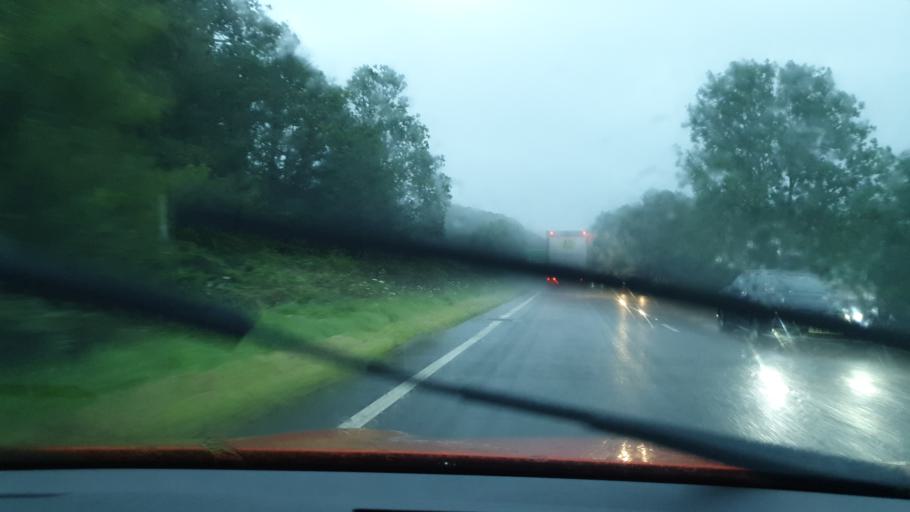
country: GB
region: England
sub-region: Cumbria
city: Ulverston
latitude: 54.2498
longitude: -3.0195
